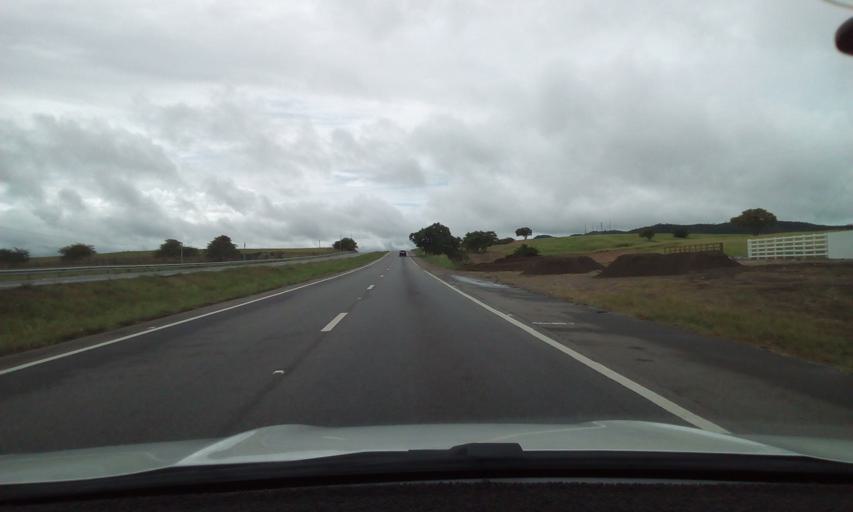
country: BR
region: Paraiba
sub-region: Gurinhem
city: Gurinhem
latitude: -7.1874
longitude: -35.4557
